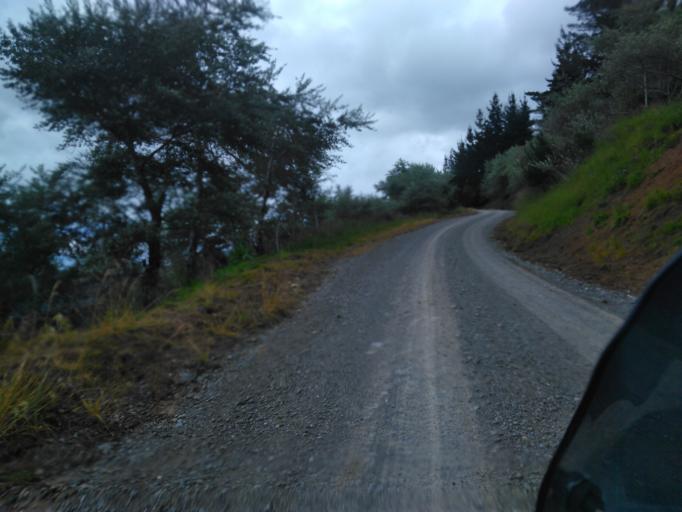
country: NZ
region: Gisborne
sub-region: Gisborne District
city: Gisborne
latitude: -38.0508
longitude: 178.0909
